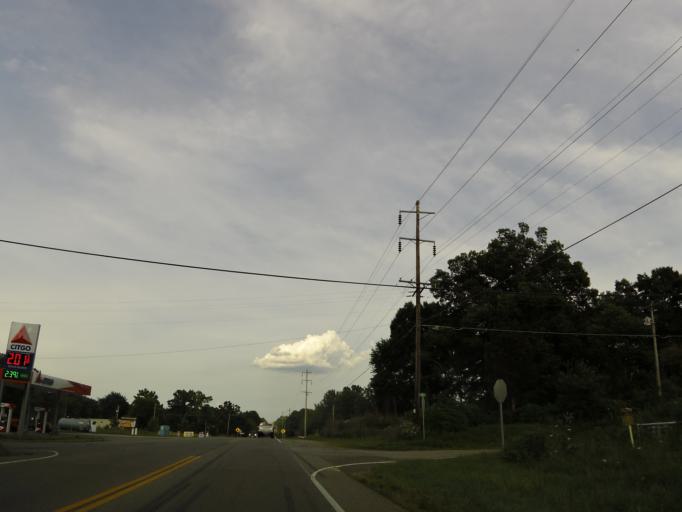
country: US
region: Tennessee
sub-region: Humphreys County
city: McEwen
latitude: 36.0914
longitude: -87.5205
